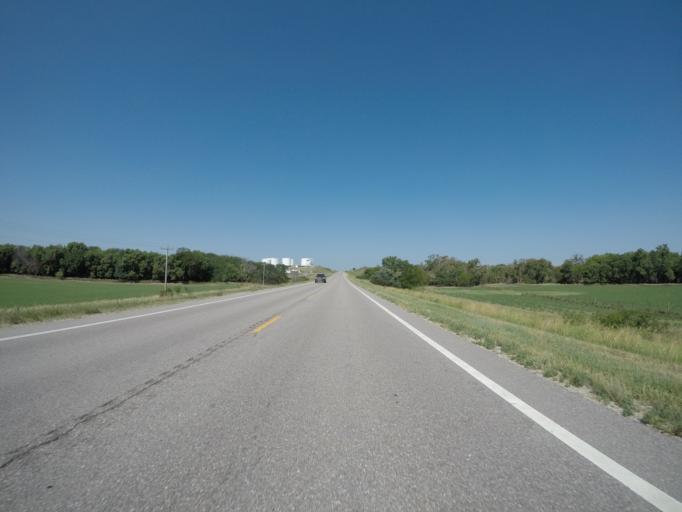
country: US
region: Kansas
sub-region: Cloud County
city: Concordia
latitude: 39.3647
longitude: -97.6233
